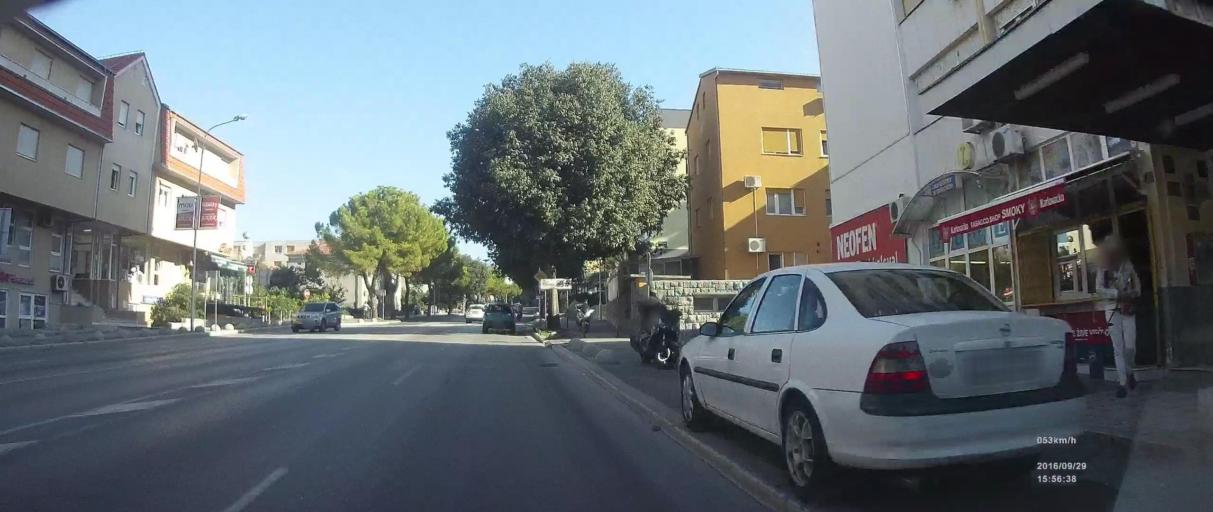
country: HR
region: Splitsko-Dalmatinska
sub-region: Grad Split
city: Split
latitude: 43.5168
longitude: 16.4460
